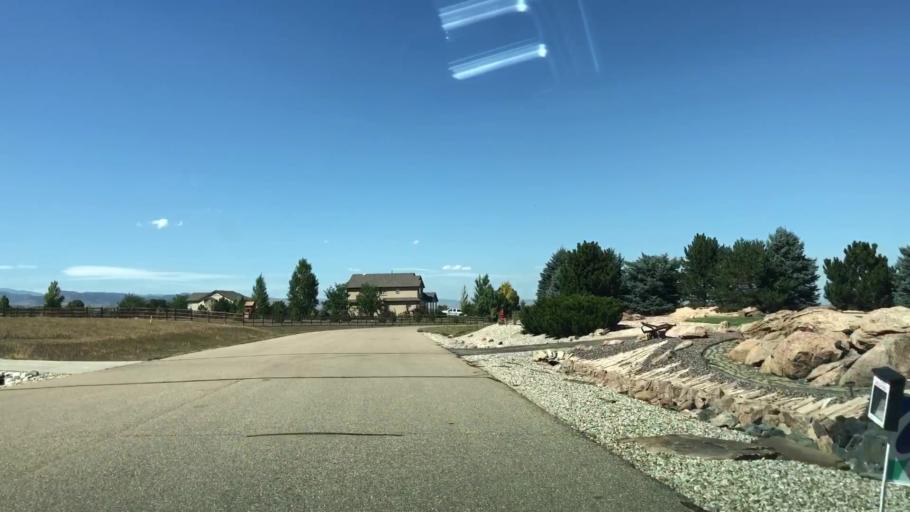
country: US
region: Colorado
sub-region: Weld County
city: Windsor
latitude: 40.4457
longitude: -104.9580
